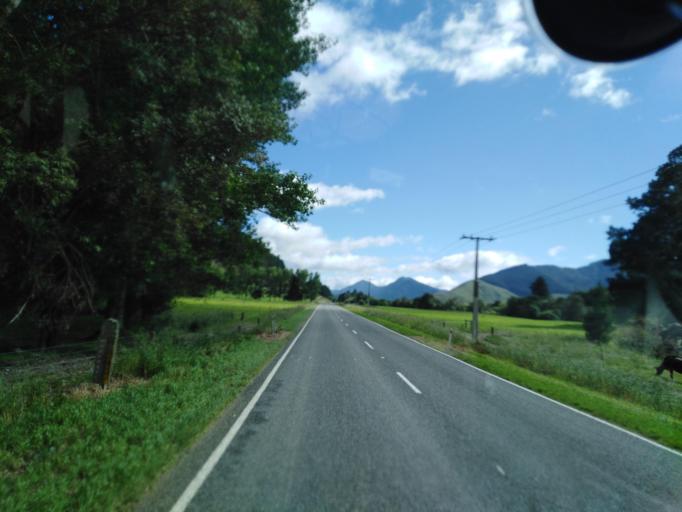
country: NZ
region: Nelson
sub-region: Nelson City
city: Nelson
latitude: -41.2656
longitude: 173.5730
